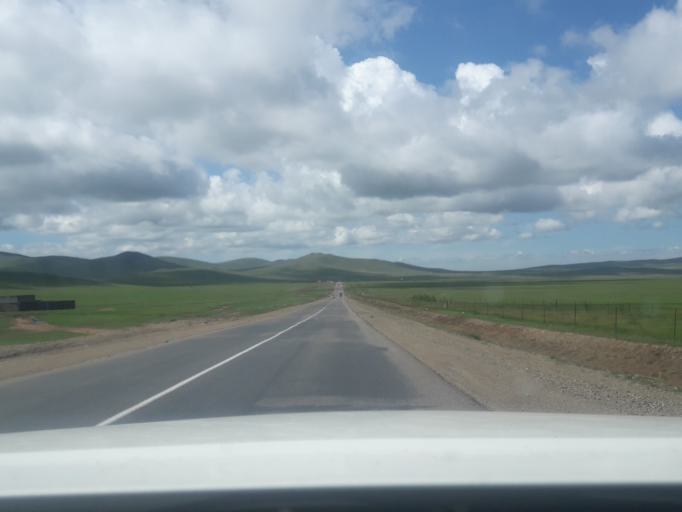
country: MN
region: Central Aimak
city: Altanbulag
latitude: 47.9006
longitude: 106.4672
